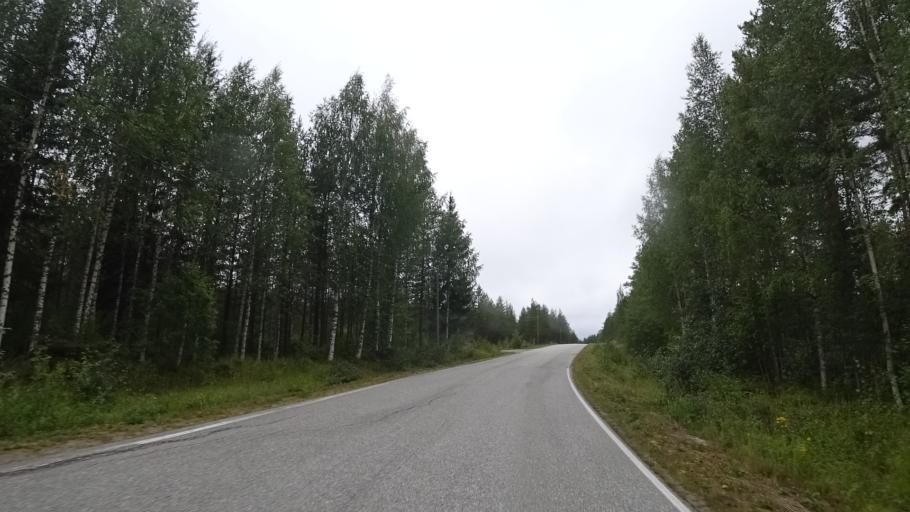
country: FI
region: North Karelia
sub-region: Pielisen Karjala
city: Lieksa
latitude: 63.3228
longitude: 30.2096
